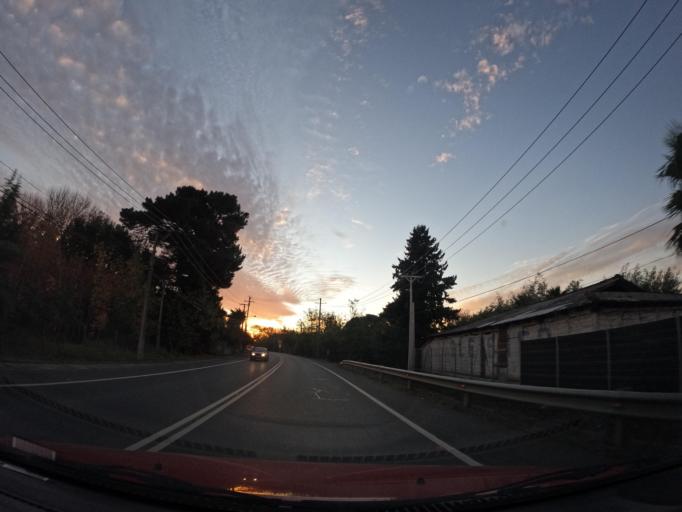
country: CL
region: Biobio
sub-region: Provincia de Nuble
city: Chillan
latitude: -36.6426
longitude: -72.0189
